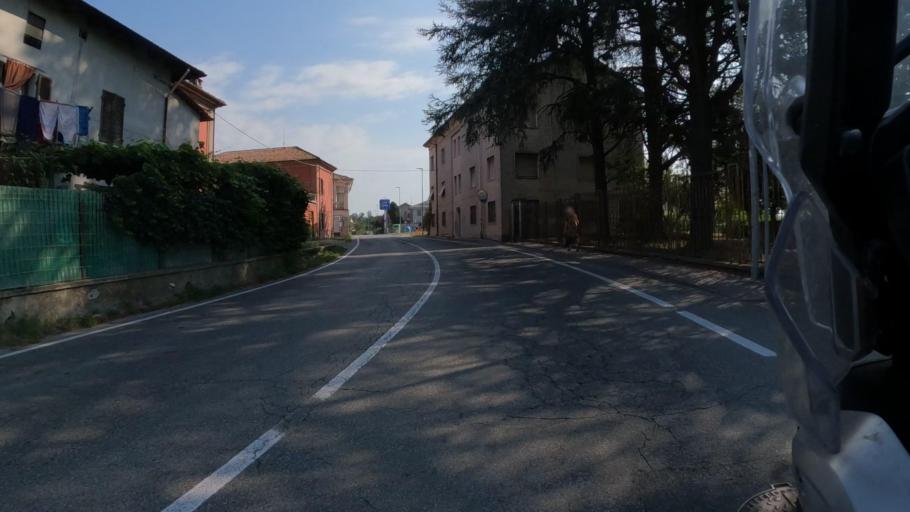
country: IT
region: Piedmont
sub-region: Provincia di Asti
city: Nizza Monferrato
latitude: 44.7760
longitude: 8.3625
